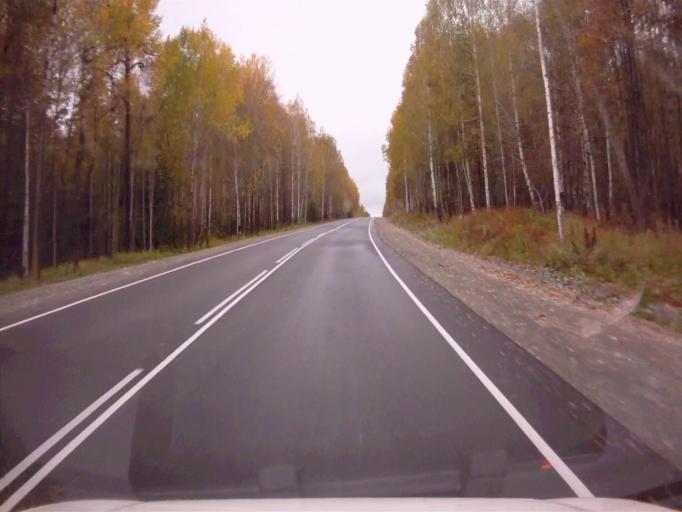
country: RU
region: Chelyabinsk
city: Nyazepetrovsk
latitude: 56.0650
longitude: 59.7025
